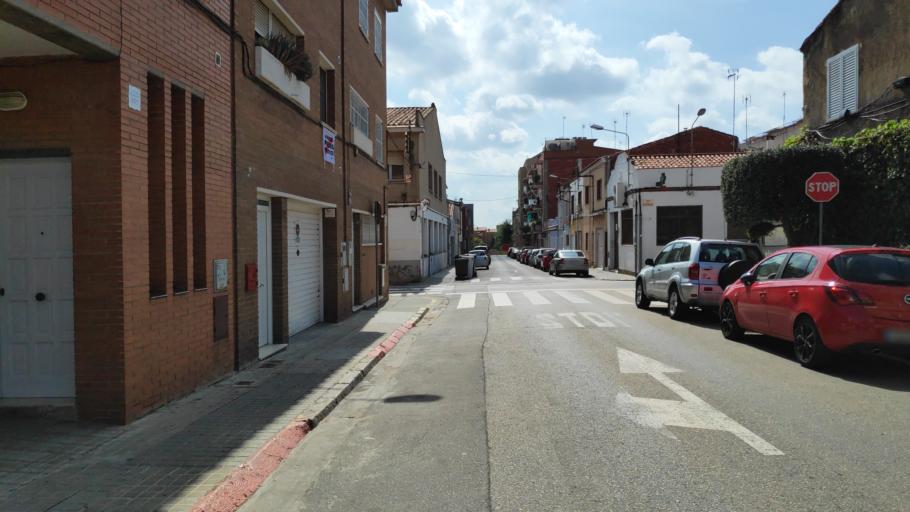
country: ES
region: Catalonia
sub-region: Provincia de Barcelona
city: Sabadell
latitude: 41.5417
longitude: 2.0957
